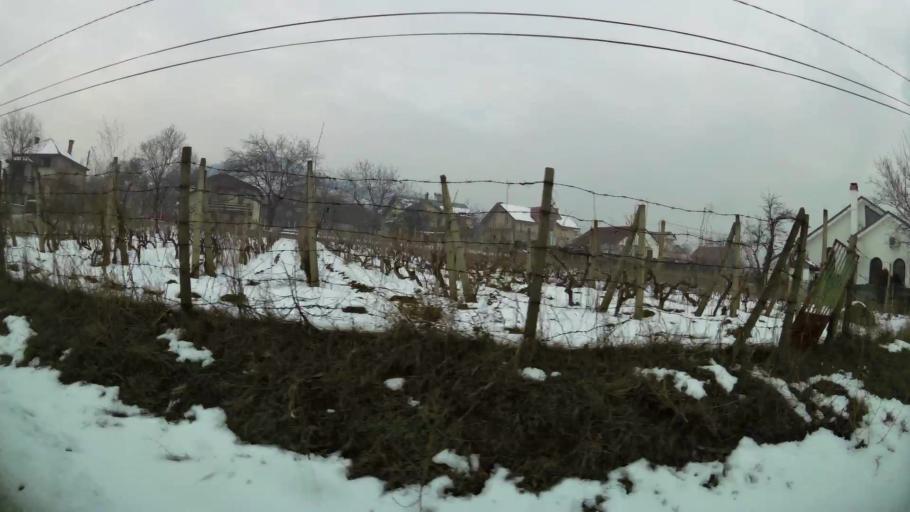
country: MK
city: Kondovo
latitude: 42.0436
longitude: 21.3426
